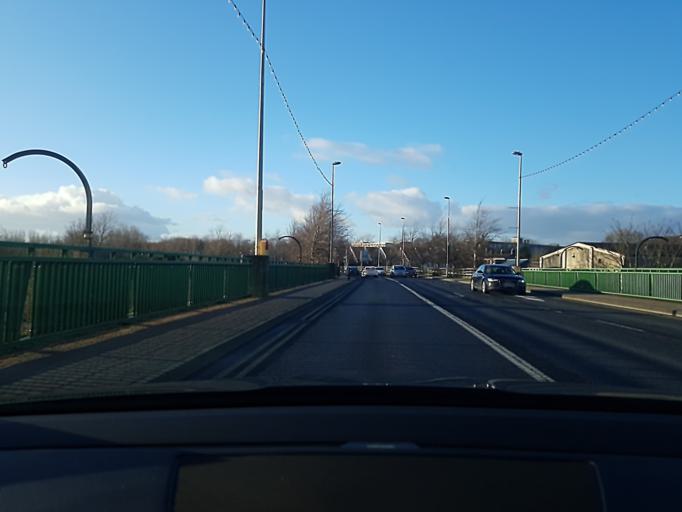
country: IE
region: Munster
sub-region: County Limerick
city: Luimneach
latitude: 52.6625
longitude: -8.6357
